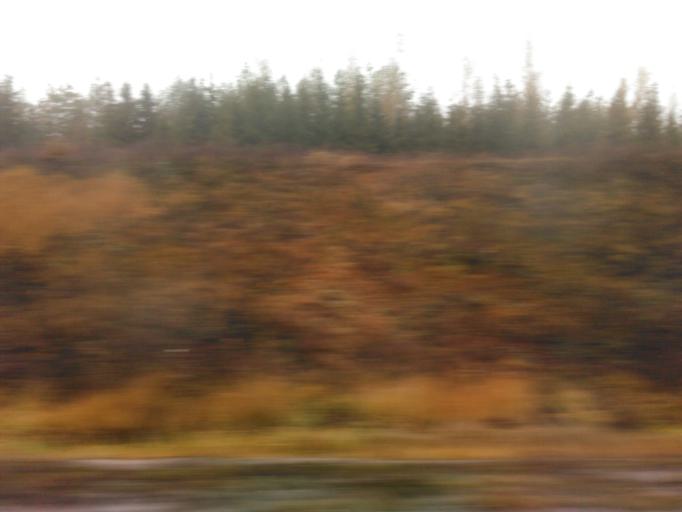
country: RU
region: Tatarstan
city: Sviyazhsk
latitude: 55.7244
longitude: 48.7520
